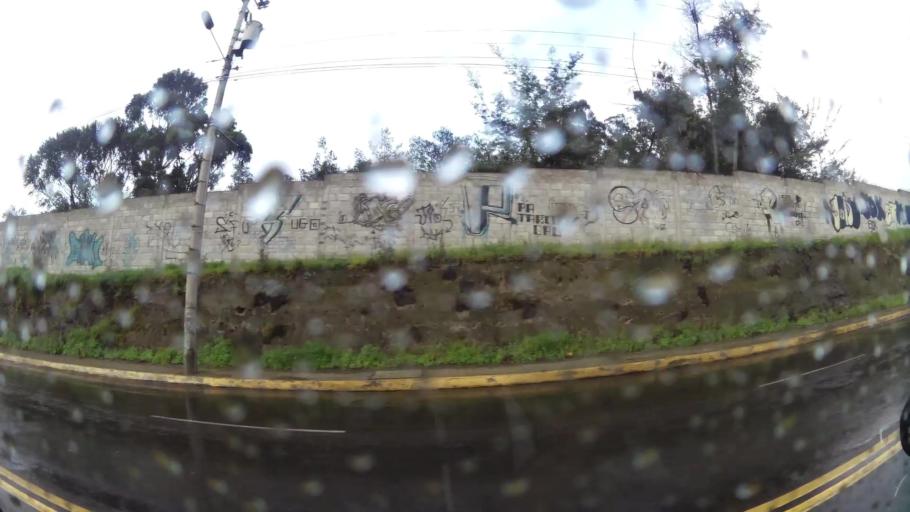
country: EC
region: Pichincha
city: Quito
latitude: -0.0956
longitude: -78.4975
